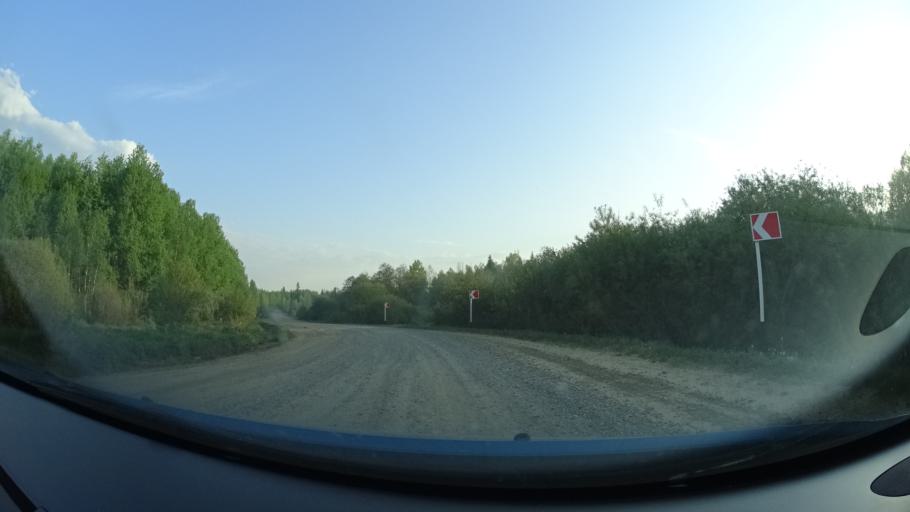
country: RU
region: Perm
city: Kuyeda
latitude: 56.6212
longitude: 55.7106
